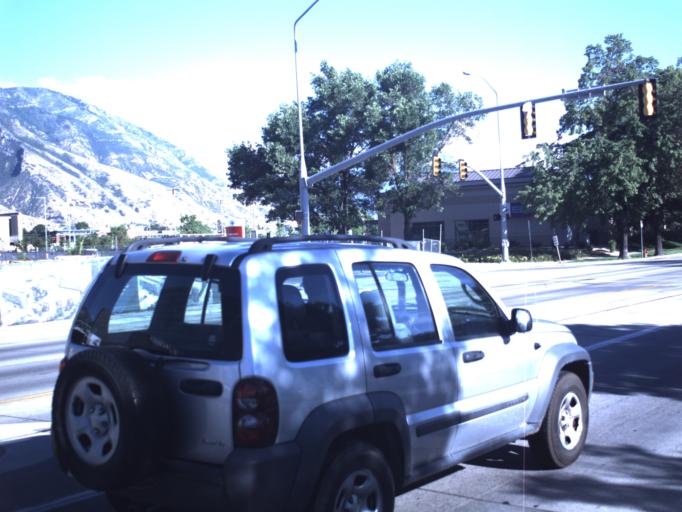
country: US
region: Utah
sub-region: Utah County
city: Provo
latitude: 40.2468
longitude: -111.6675
